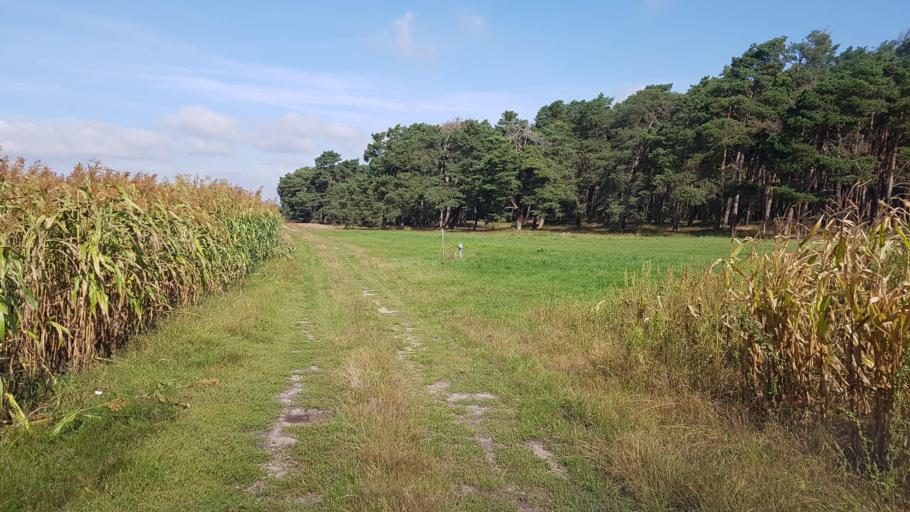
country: DE
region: Brandenburg
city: Hohenbucko
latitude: 51.7221
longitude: 13.4846
